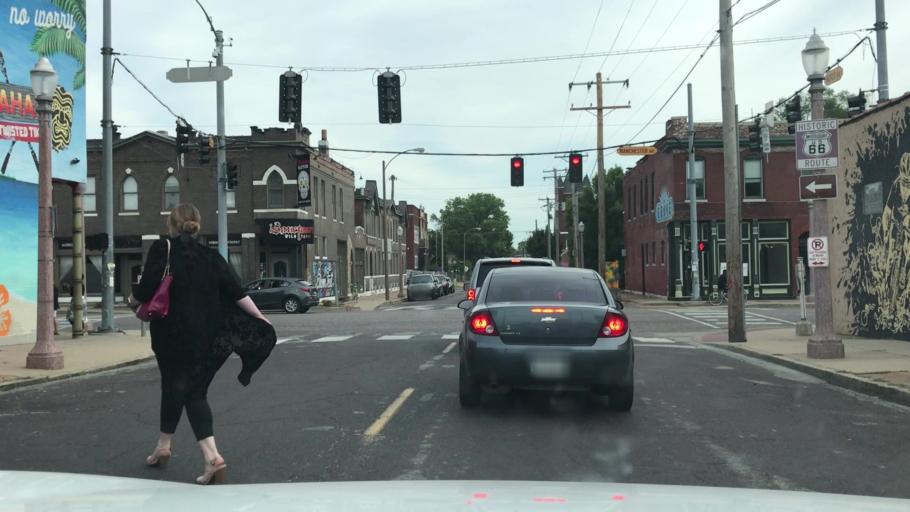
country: US
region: Missouri
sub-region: City of Saint Louis
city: St. Louis
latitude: 38.6277
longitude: -90.2542
